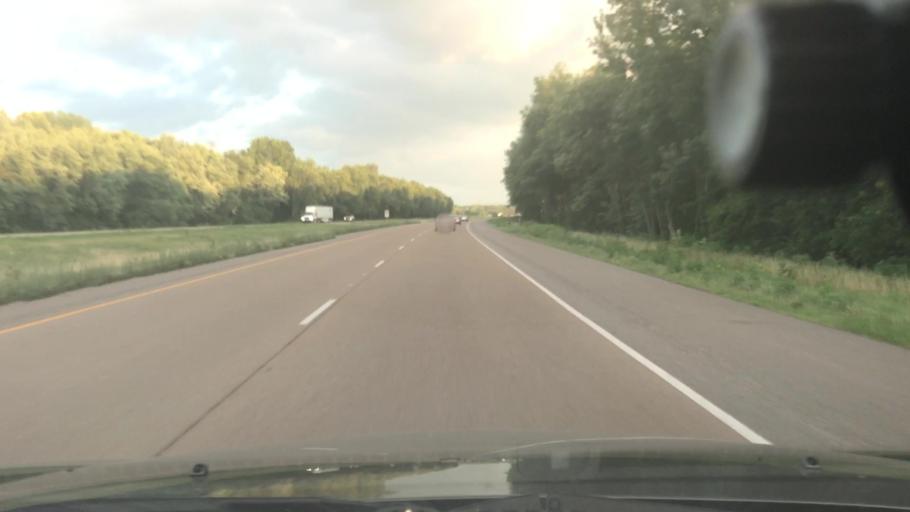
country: US
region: Illinois
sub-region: Washington County
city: Okawville
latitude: 38.4731
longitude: -89.5763
